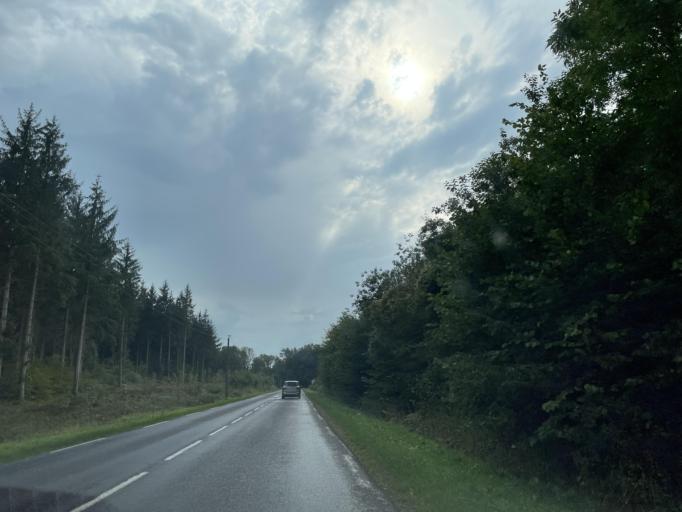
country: FR
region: Haute-Normandie
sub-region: Departement de la Seine-Maritime
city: Neufchatel-en-Bray
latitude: 49.7652
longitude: 1.4278
